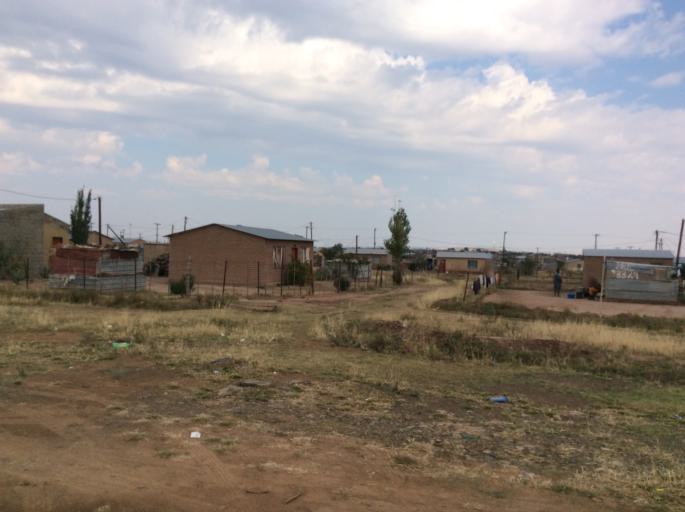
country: LS
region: Mafeteng
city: Mafeteng
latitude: -29.7092
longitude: 27.0104
